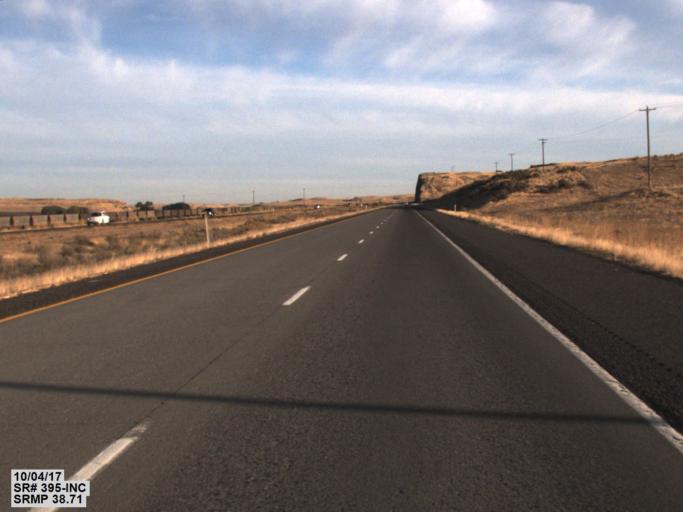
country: US
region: Washington
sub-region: Franklin County
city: Basin City
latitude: 46.4673
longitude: -119.0120
